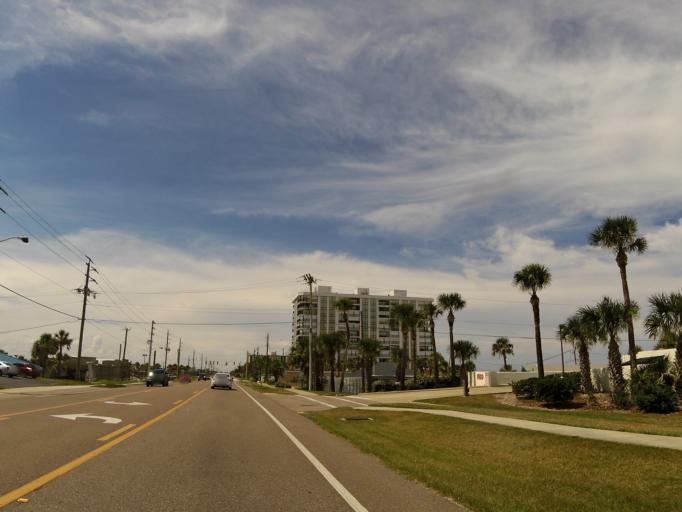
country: US
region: Florida
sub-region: Volusia County
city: Ormond-by-the-Sea
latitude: 29.3215
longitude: -81.0544
